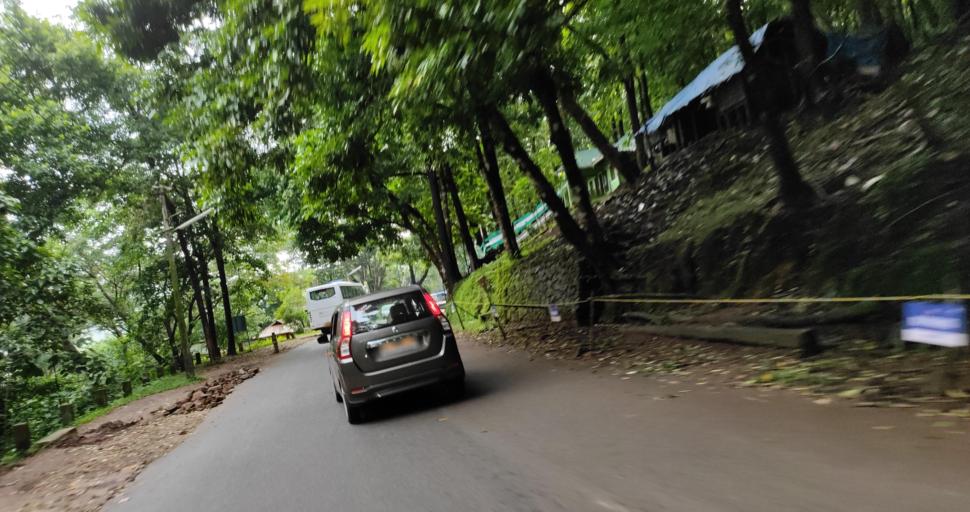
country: IN
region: Kerala
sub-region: Ernakulam
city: Angamali
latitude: 10.2882
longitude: 76.5663
